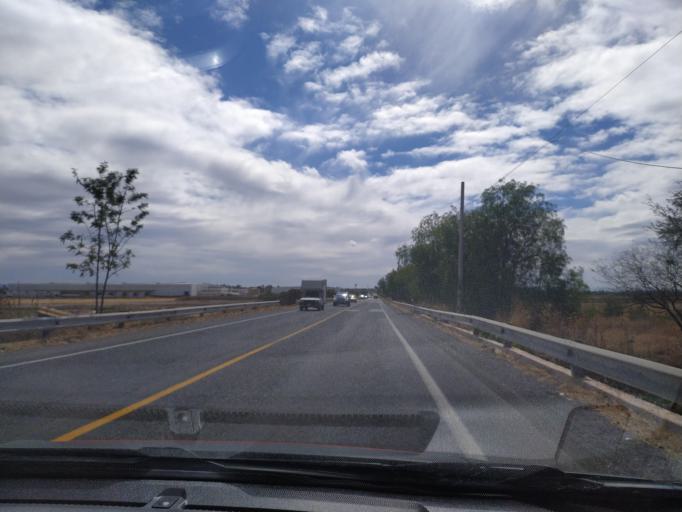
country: LA
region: Oudomxai
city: Muang La
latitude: 21.0090
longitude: 101.8295
